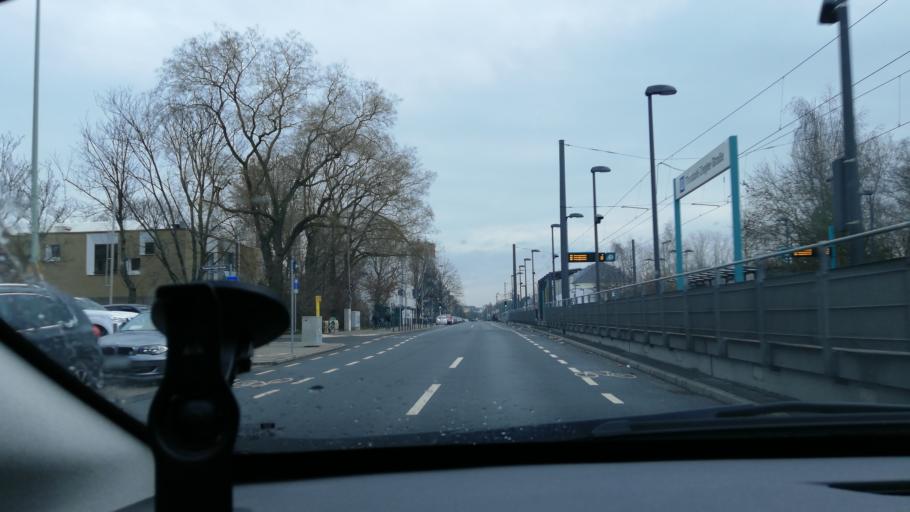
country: DE
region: Hesse
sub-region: Regierungsbezirk Darmstadt
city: Frankfurt am Main
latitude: 50.1483
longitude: 8.6898
